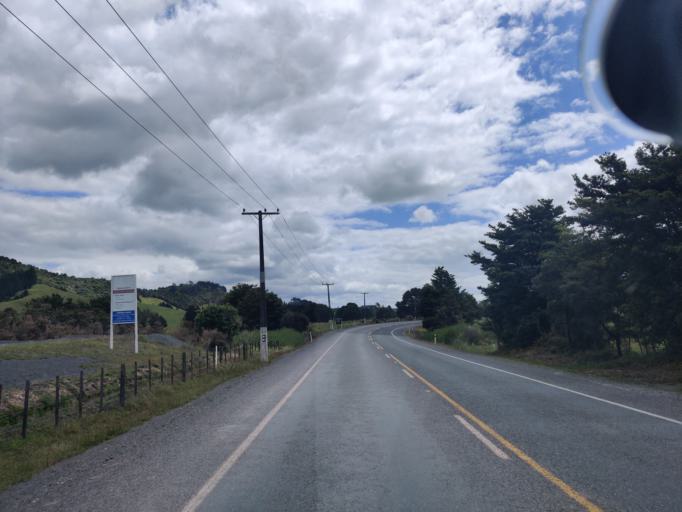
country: NZ
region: Northland
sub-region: Far North District
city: Kerikeri
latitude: -35.2942
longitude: 173.9817
